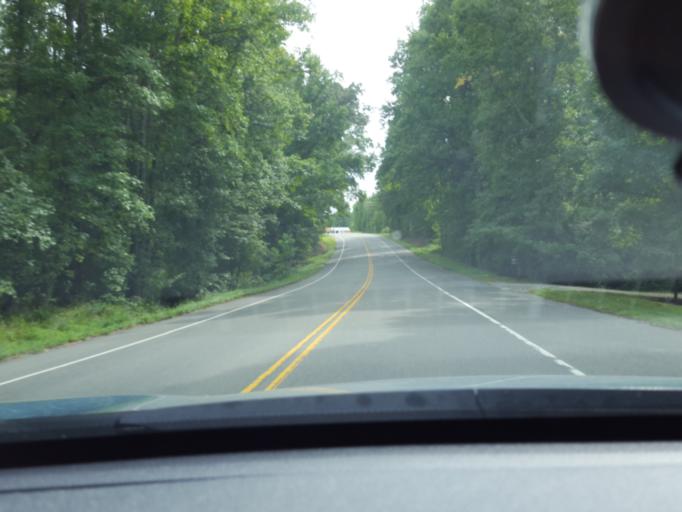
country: US
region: Virginia
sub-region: Hanover County
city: Hanover
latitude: 37.7106
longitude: -77.3822
